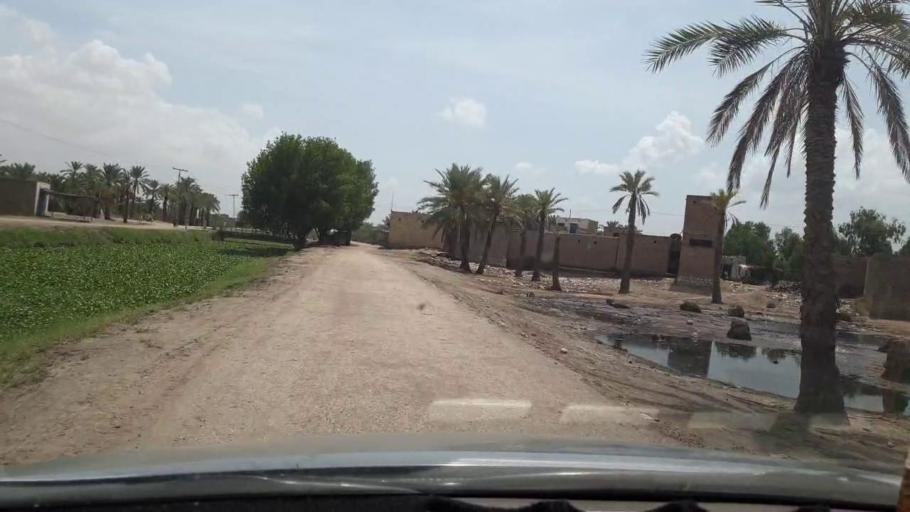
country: PK
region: Sindh
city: Khairpur
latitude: 27.4516
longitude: 68.7873
